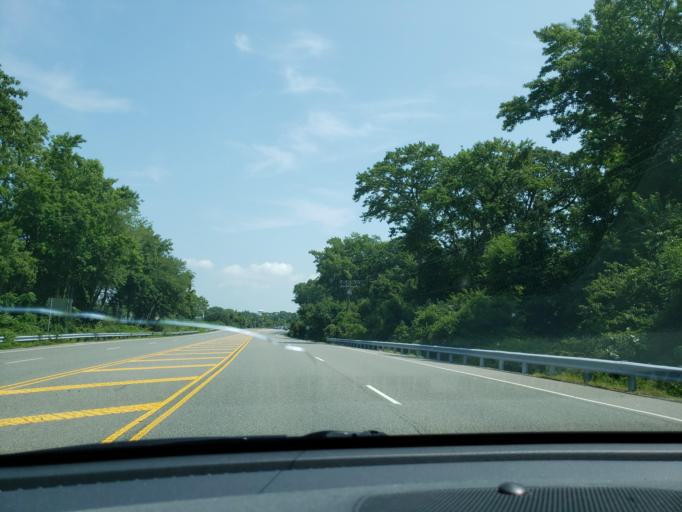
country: US
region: New Jersey
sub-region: Cape May County
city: North Cape May
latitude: 38.9732
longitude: -74.9395
